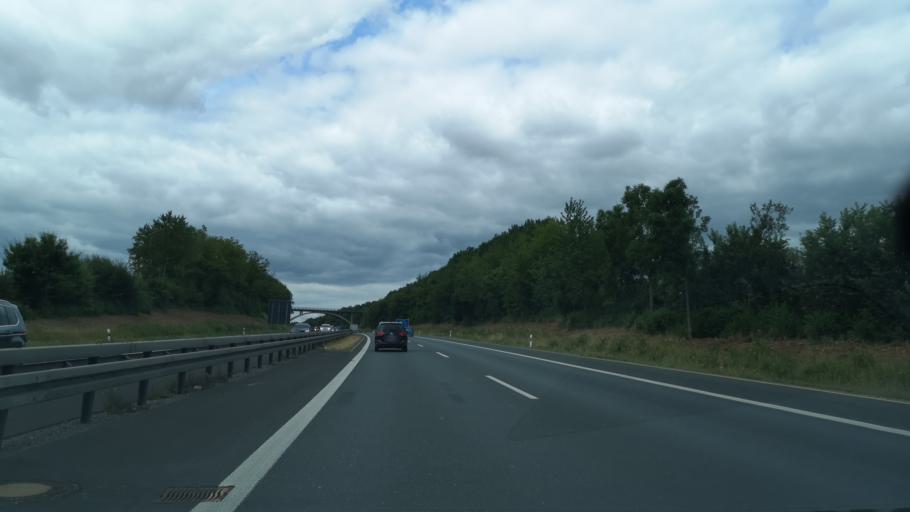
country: DE
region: Bavaria
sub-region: Regierungsbezirk Unterfranken
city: Wasserlosen
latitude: 50.0688
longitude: 10.0406
